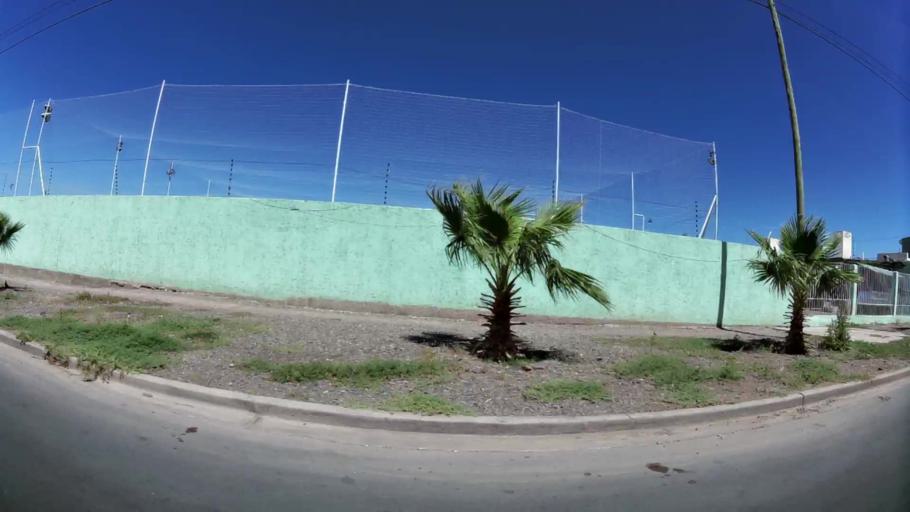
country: AR
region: Mendoza
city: Las Heras
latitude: -32.8462
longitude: -68.8556
